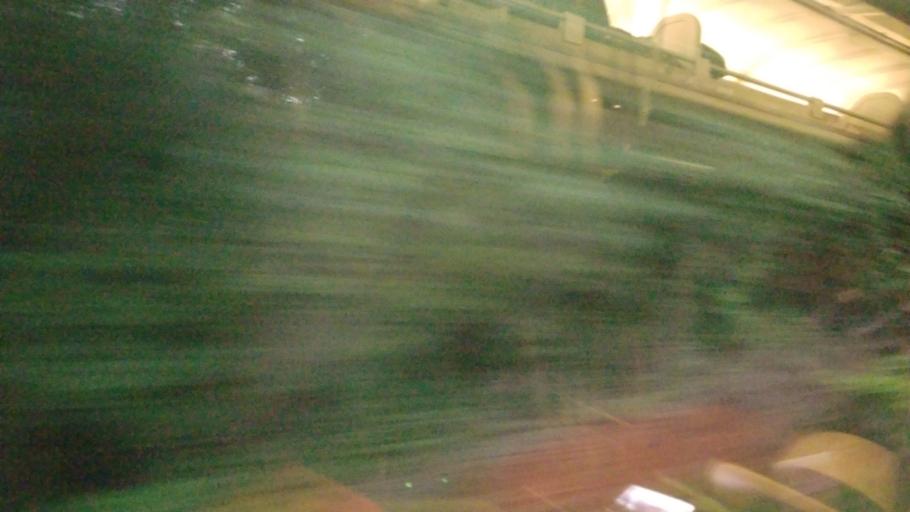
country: US
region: Virginia
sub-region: Orange County
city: Orange
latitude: 38.2589
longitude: -78.1096
